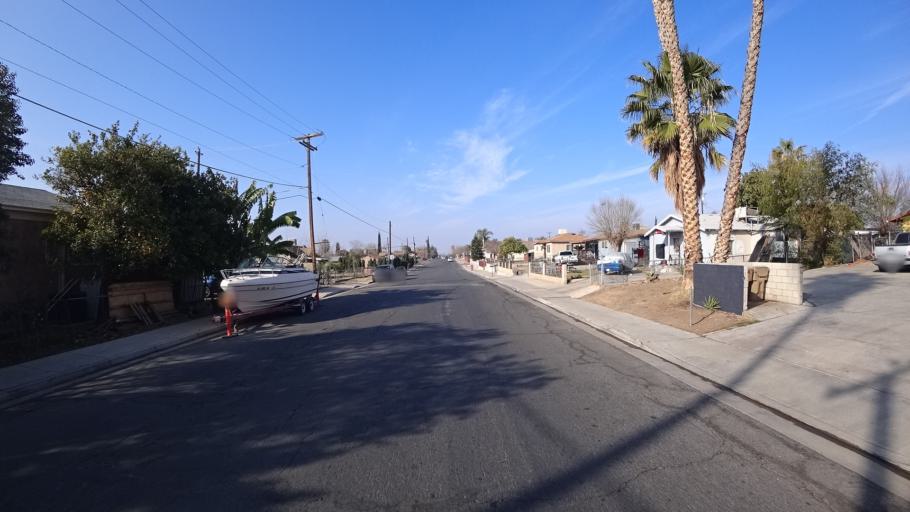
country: US
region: California
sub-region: Kern County
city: Bakersfield
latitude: 35.3939
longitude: -118.9794
